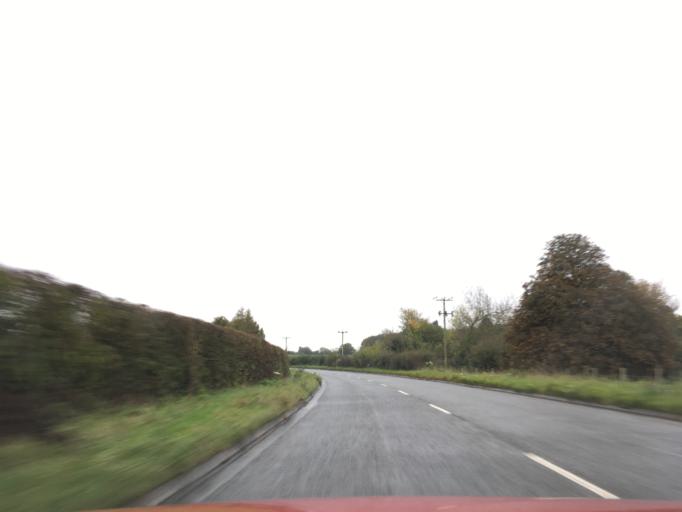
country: GB
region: England
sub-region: West Berkshire
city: Wickham
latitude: 51.4567
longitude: -1.4721
